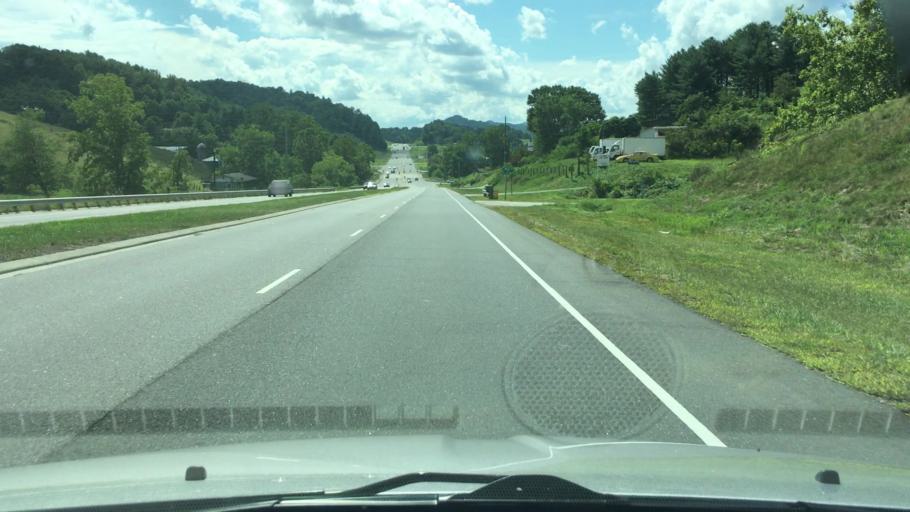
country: US
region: North Carolina
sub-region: Yancey County
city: Burnsville
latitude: 35.9127
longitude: -82.3429
